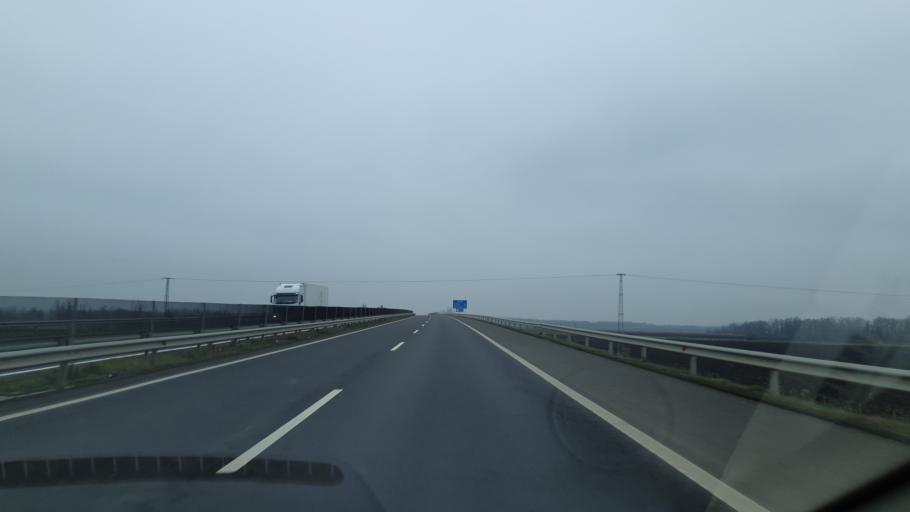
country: HU
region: Hajdu-Bihar
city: Hajdunanas
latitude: 47.8820
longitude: 21.4091
